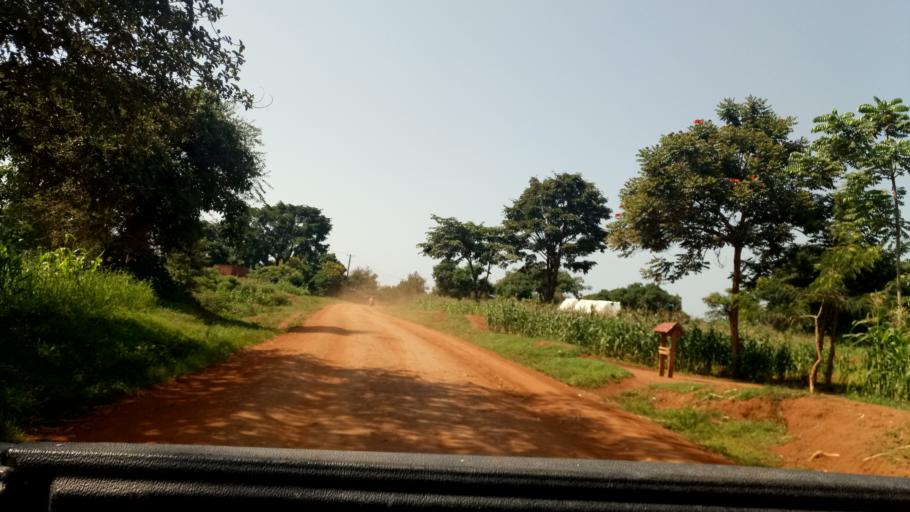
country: UG
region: Eastern Region
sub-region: Kaliro District
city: Kaliro
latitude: 0.9629
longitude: 33.4693
